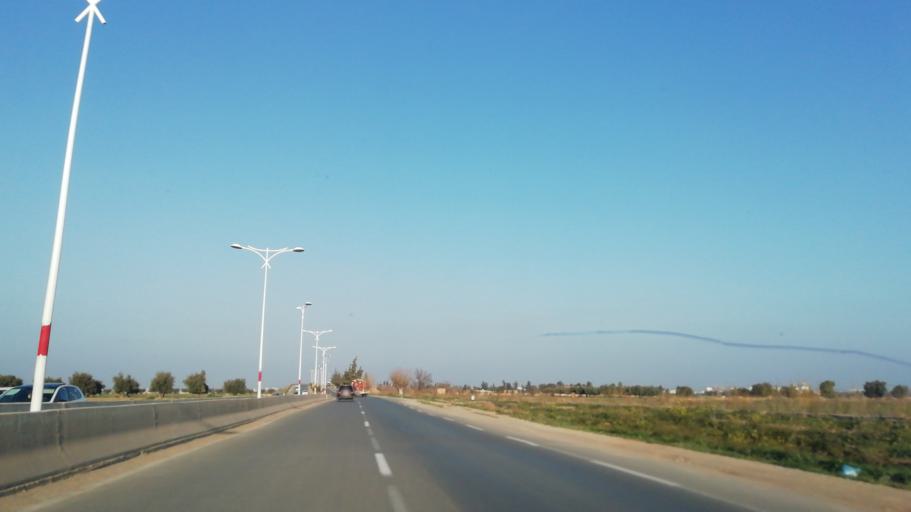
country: DZ
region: Sidi Bel Abbes
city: Sidi Bel Abbes
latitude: 35.1712
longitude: -0.6797
